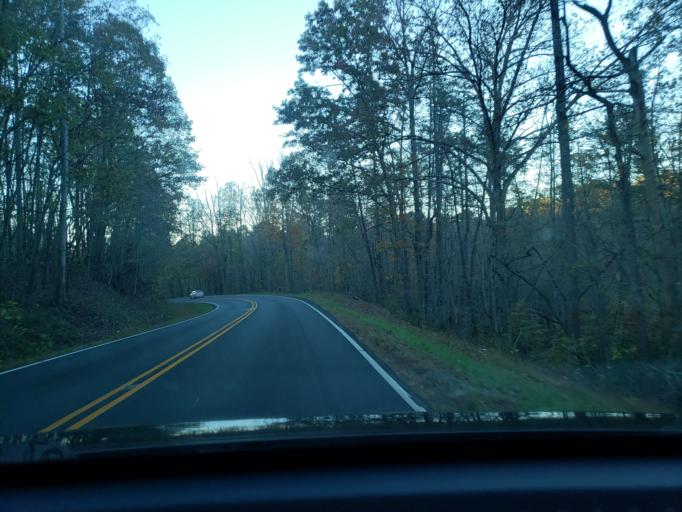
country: US
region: North Carolina
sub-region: Stokes County
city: Danbury
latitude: 36.3806
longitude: -80.1858
